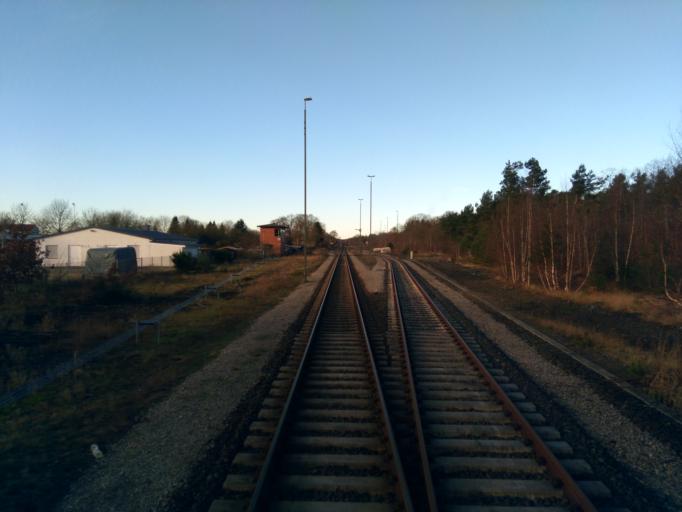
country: DE
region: Lower Saxony
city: Munster
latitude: 52.9919
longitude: 10.1039
